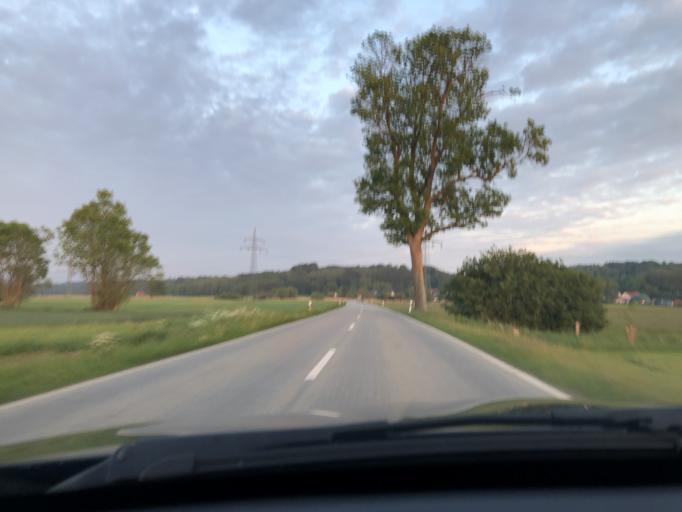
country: DE
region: Bavaria
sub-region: Upper Bavaria
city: Wolfersdorf
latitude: 48.4466
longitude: 11.7170
